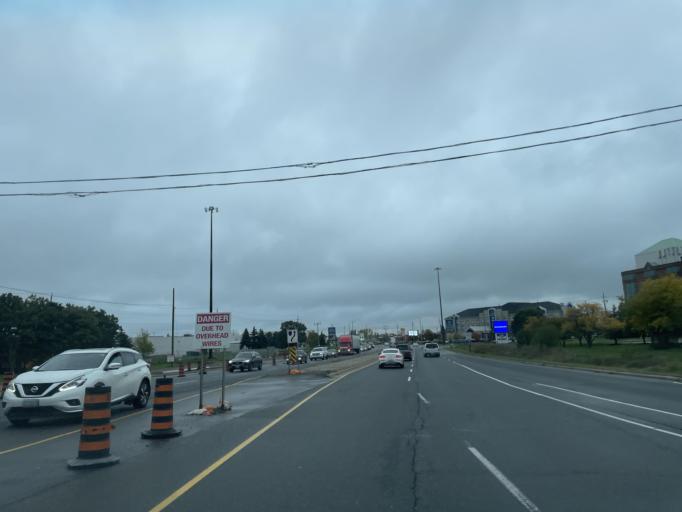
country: CA
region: Ontario
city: Cambridge
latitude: 43.4124
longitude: -80.3281
